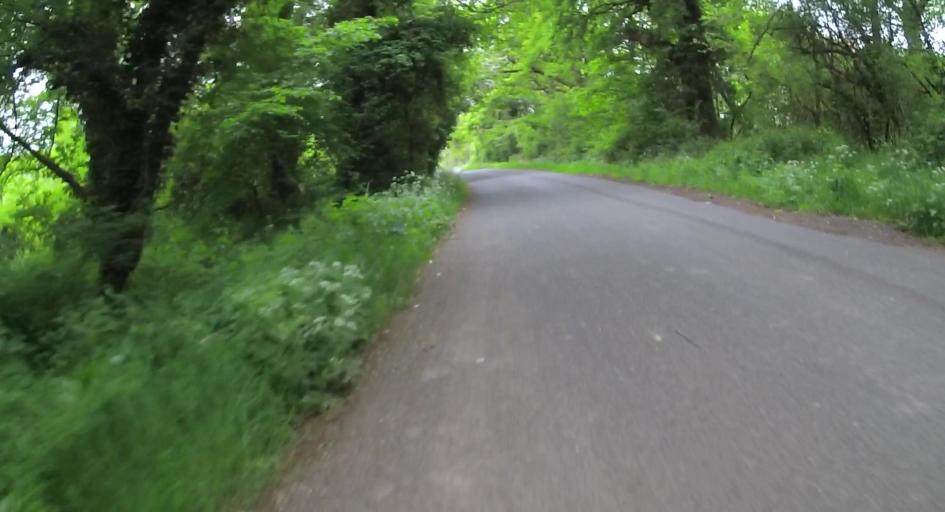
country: GB
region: England
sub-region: West Berkshire
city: Stratfield Mortimer
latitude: 51.3660
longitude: -1.0353
